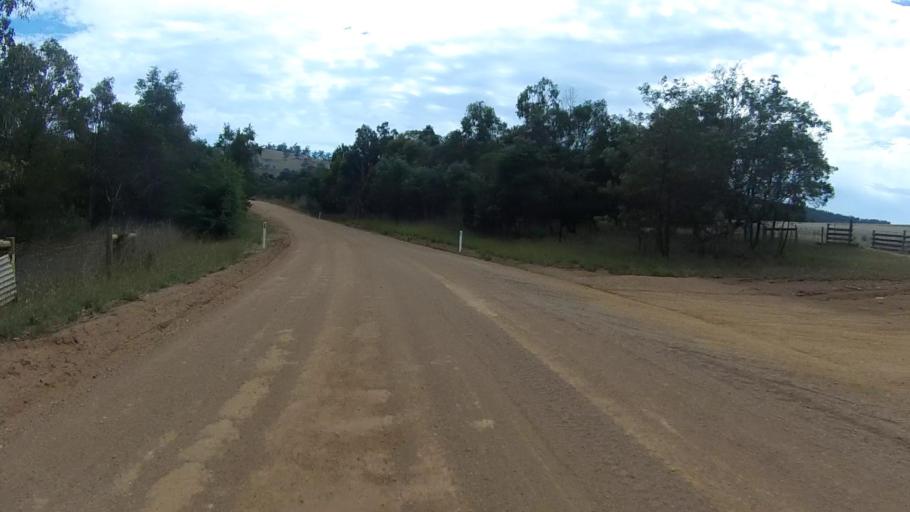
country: AU
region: Tasmania
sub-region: Sorell
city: Sorell
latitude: -42.6978
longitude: 147.4621
